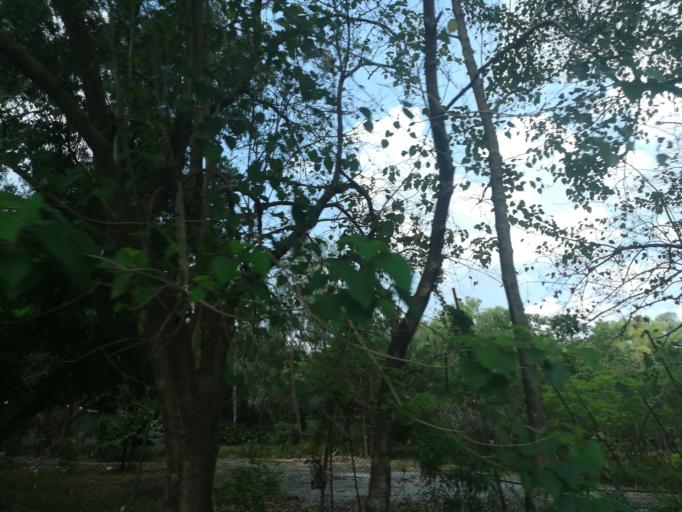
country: NG
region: Abuja Federal Capital Territory
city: Abuja
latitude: 9.0786
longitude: 7.4182
